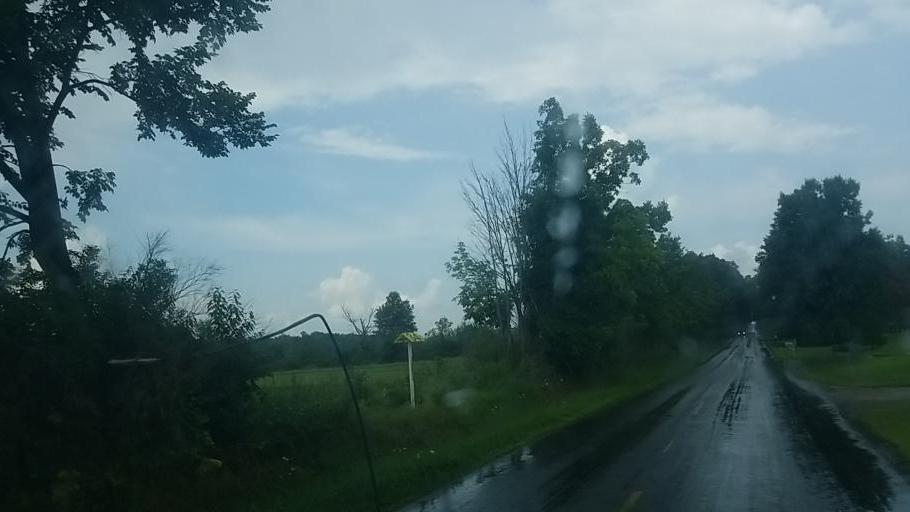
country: US
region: Ohio
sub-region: Lorain County
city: Lagrange
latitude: 41.1796
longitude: -82.0534
